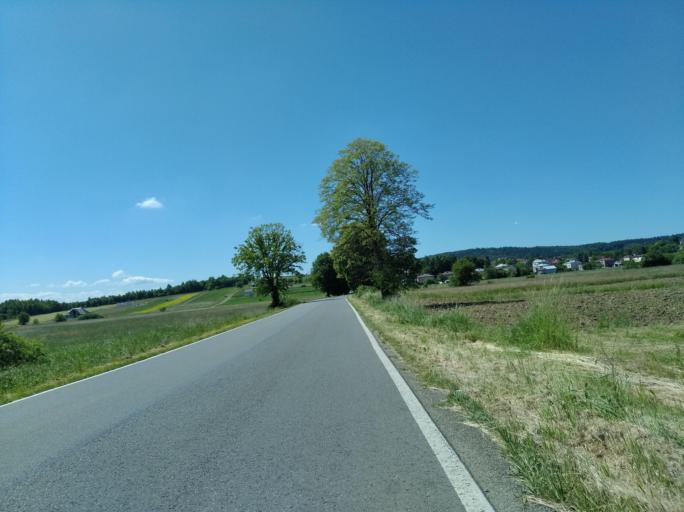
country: PL
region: Subcarpathian Voivodeship
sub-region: Powiat krosnienski
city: Chorkowka
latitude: 49.6561
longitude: 21.6845
